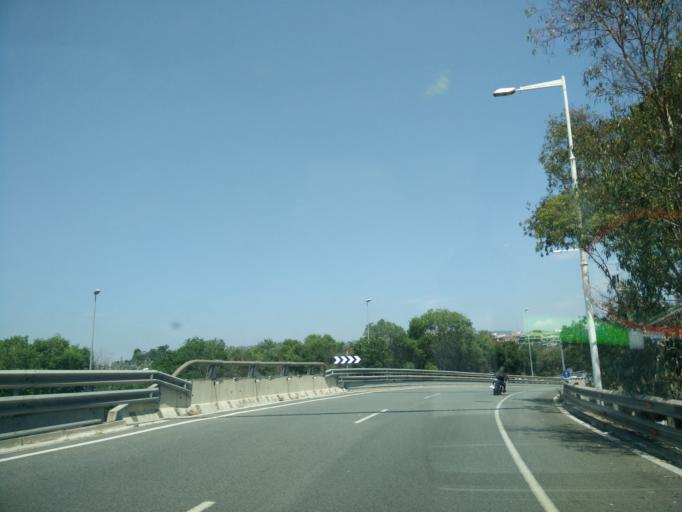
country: ES
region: Catalonia
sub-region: Provincia de Barcelona
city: Sant Adria de Besos
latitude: 41.4247
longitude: 2.2176
